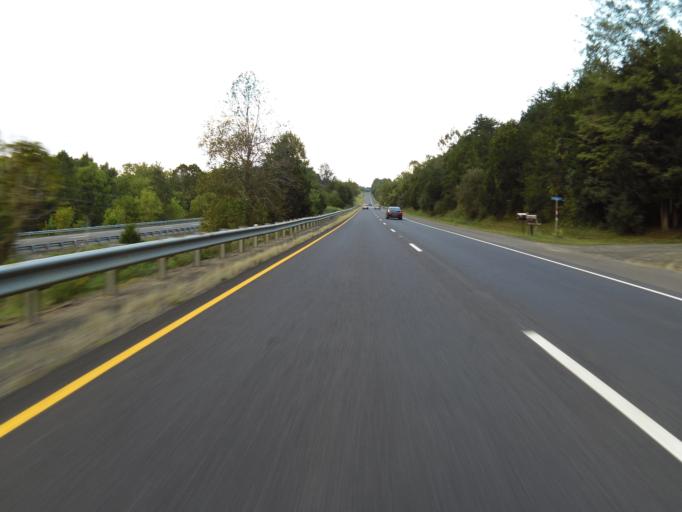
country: US
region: Virginia
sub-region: Fauquier County
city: Warrenton
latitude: 38.6822
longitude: -77.9049
